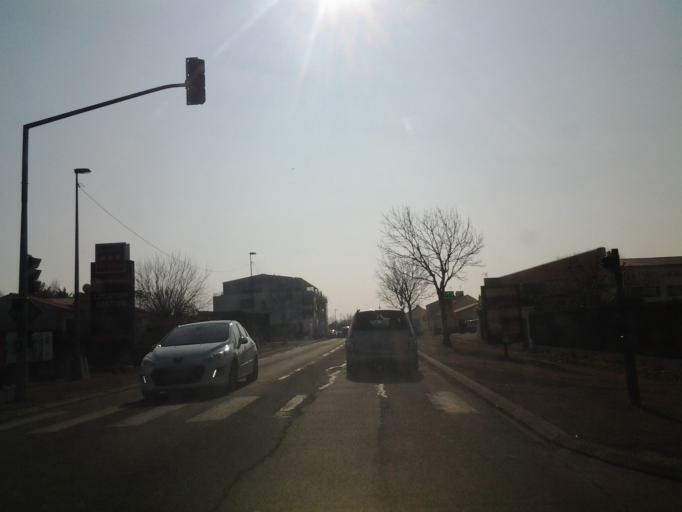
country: FR
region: Pays de la Loire
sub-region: Departement de la Vendee
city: Les Sables-d'Olonne
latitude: 46.5094
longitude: -1.7688
